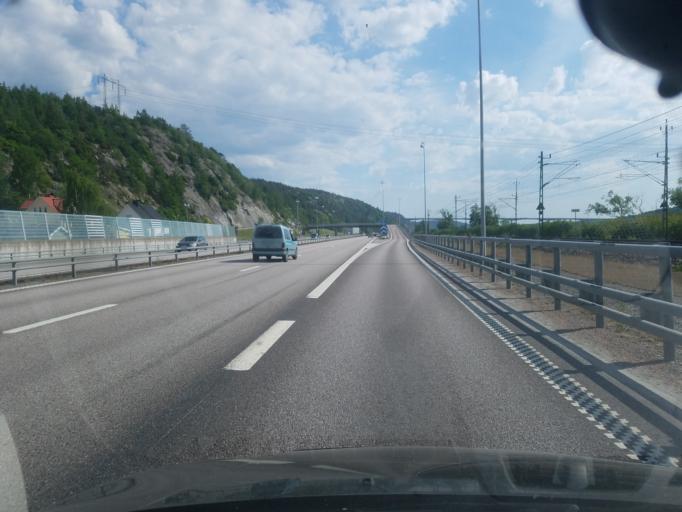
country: SE
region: Vaestra Goetaland
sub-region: Ale Kommun
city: Surte
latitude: 57.8185
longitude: 12.0148
